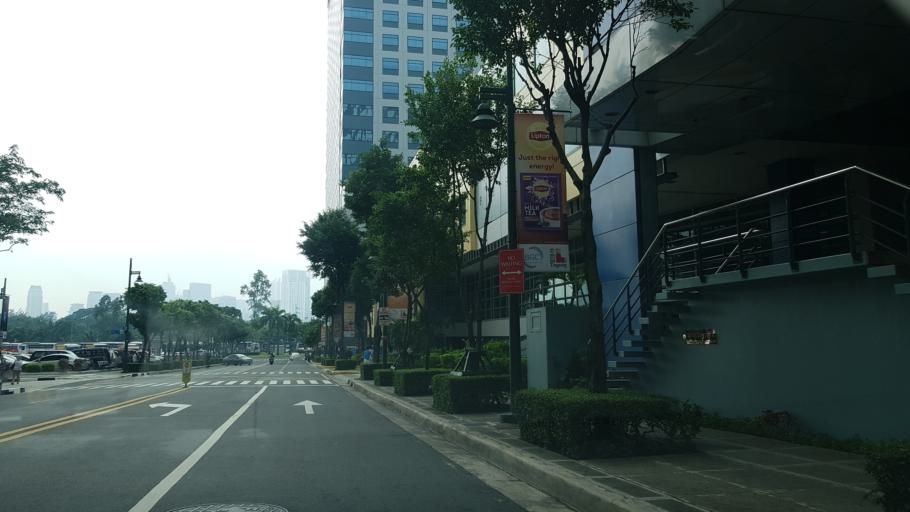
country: PH
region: Metro Manila
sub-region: Makati City
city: Makati City
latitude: 14.5546
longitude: 121.0444
